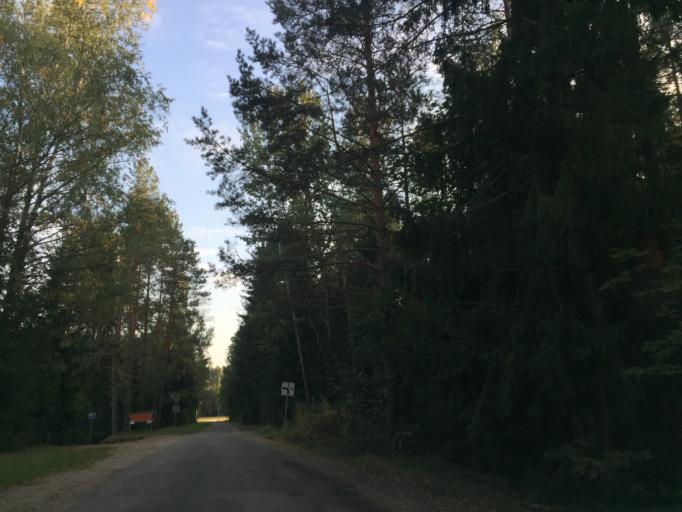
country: LV
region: Baldone
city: Baldone
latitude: 56.7709
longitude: 24.3994
